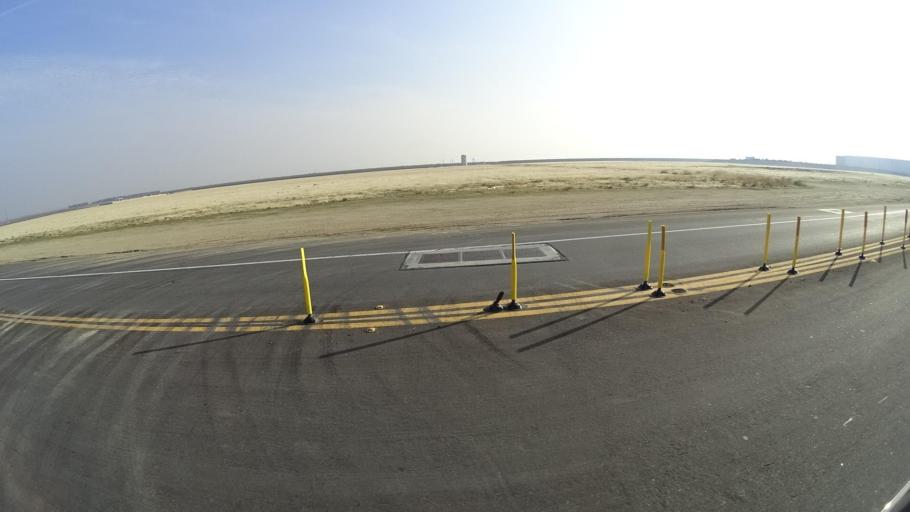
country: US
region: California
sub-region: Kern County
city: Lebec
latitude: 35.0021
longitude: -118.9434
